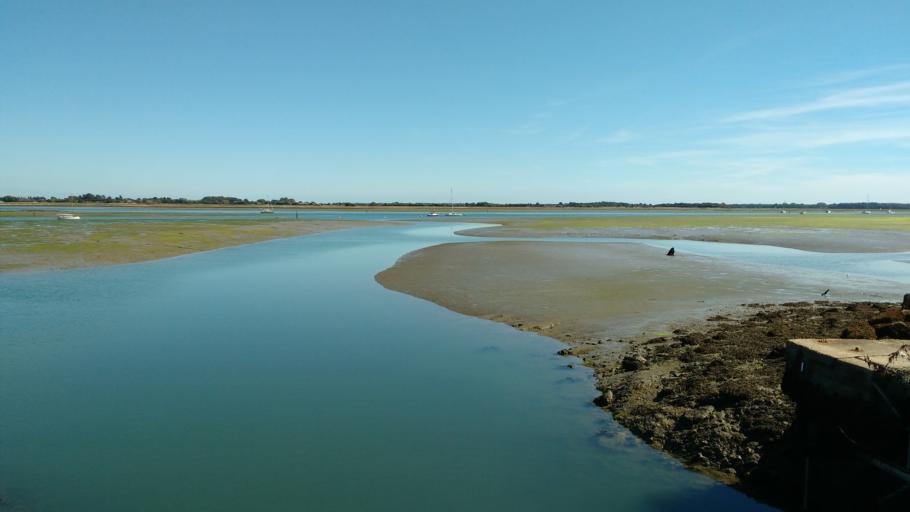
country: GB
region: England
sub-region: Hampshire
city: Emsworth
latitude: 50.8281
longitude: -0.9124
